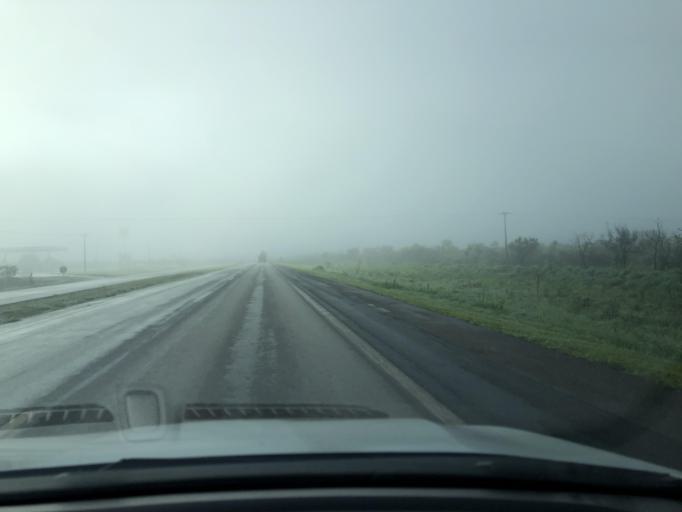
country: BR
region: Goias
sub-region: Luziania
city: Luziania
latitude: -16.2854
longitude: -47.8565
